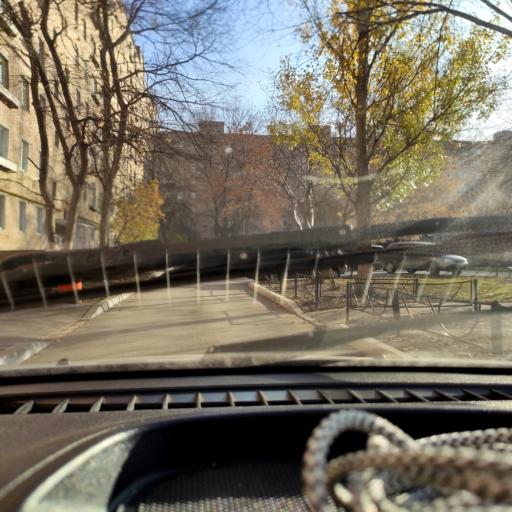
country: RU
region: Samara
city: Tol'yatti
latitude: 53.5063
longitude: 49.4268
